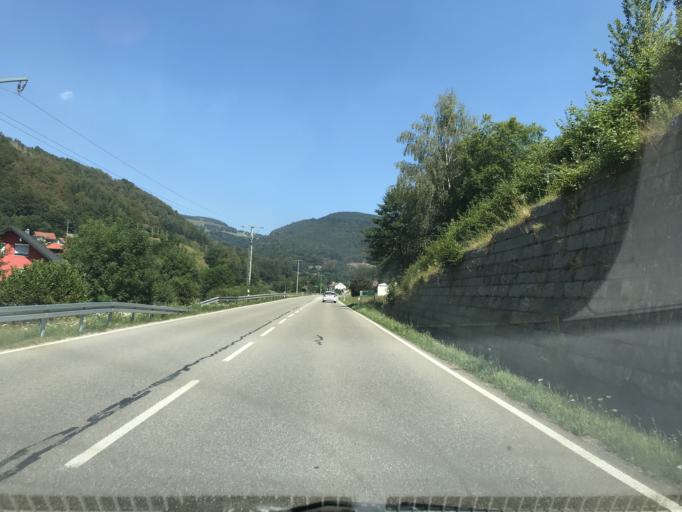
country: DE
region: Baden-Wuerttemberg
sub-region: Freiburg Region
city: Todtnau
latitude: 47.8162
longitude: 7.9387
